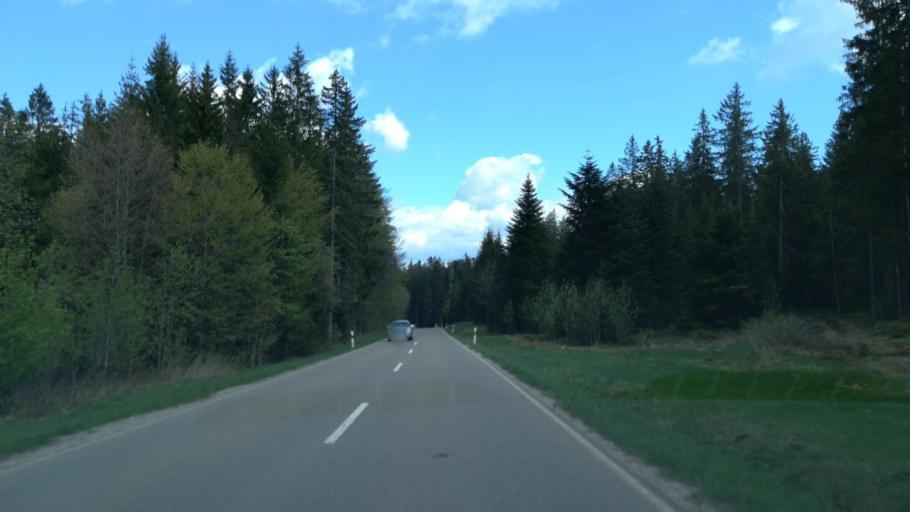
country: DE
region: Baden-Wuerttemberg
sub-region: Freiburg Region
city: Lenzkirch
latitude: 47.8305
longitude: 8.2404
